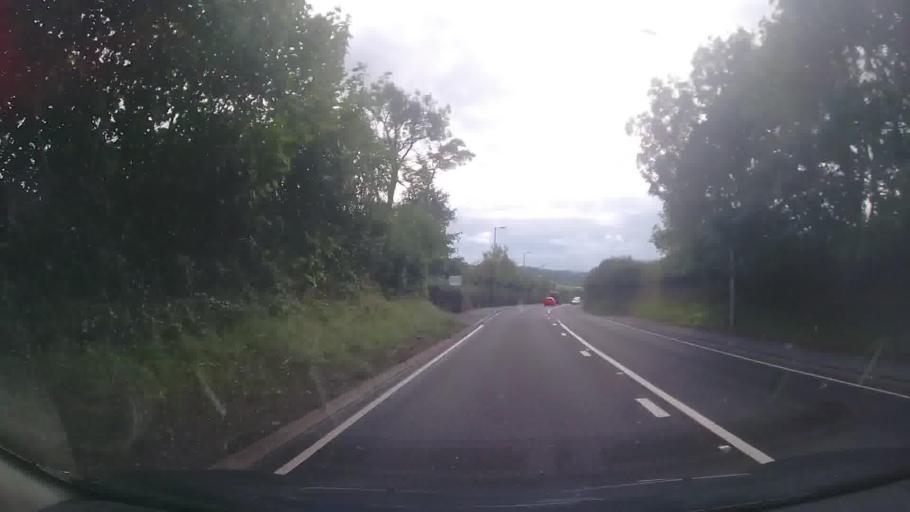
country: GB
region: Wales
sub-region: Carmarthenshire
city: Saint Clears
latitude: 51.8143
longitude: -4.5084
